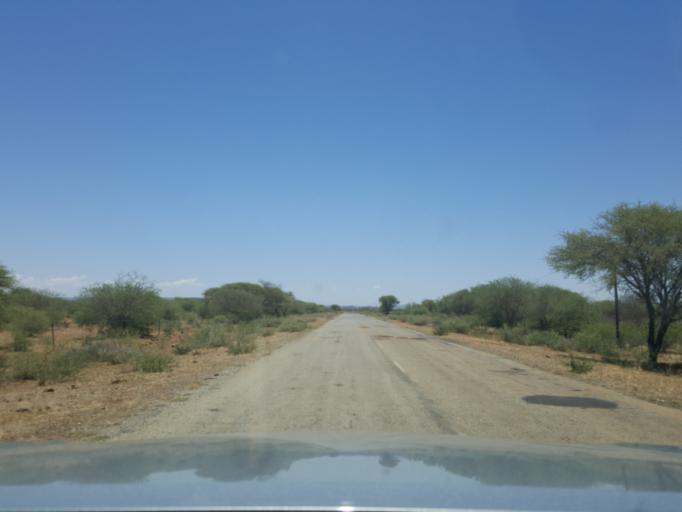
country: BW
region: South East
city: Ramotswa
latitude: -25.0162
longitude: 25.9084
